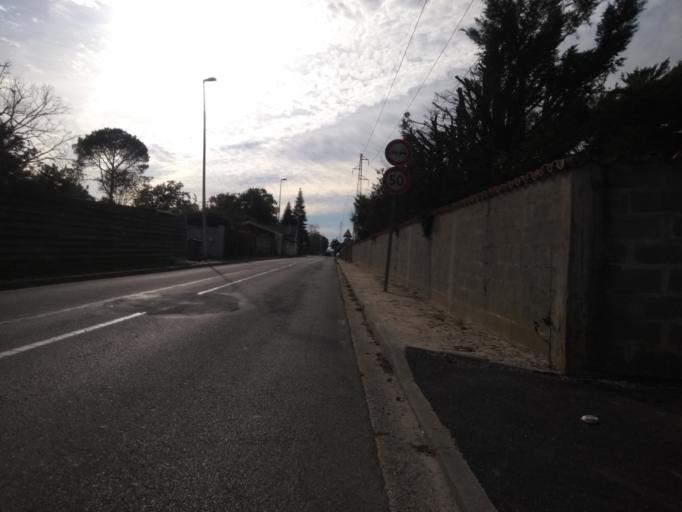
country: FR
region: Aquitaine
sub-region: Departement de la Gironde
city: Pessac
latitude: 44.7847
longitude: -0.6722
